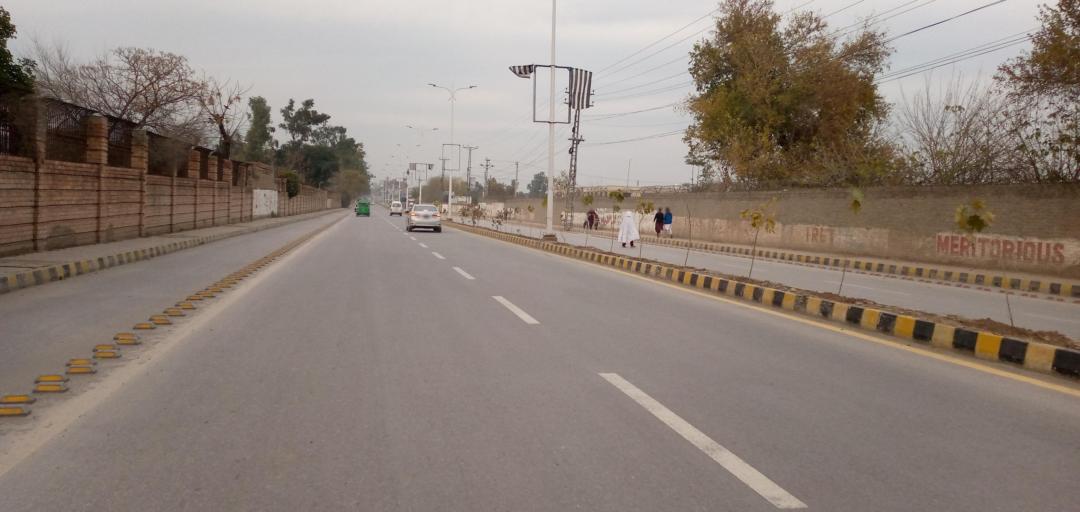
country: PK
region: Khyber Pakhtunkhwa
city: Peshawar
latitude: 34.0116
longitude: 71.4891
